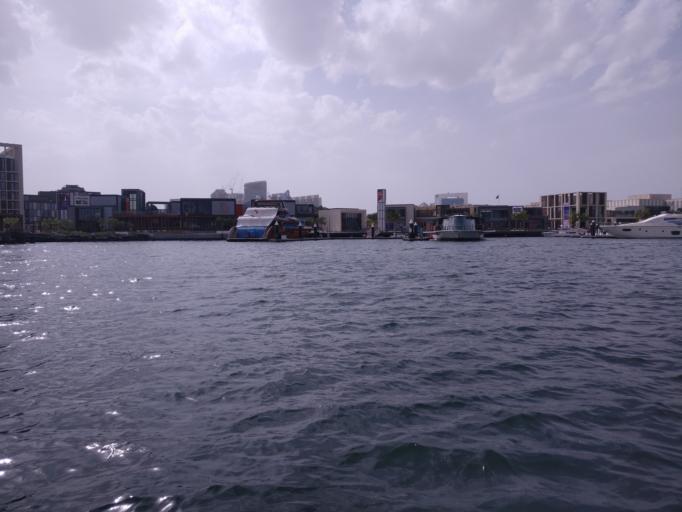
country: AE
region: Ash Shariqah
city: Sharjah
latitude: 25.2581
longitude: 55.3134
